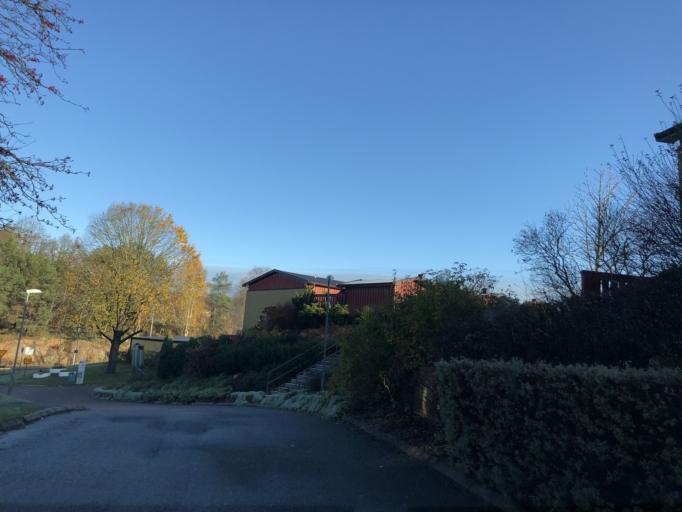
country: SE
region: Vaestra Goetaland
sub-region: Goteborg
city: Rannebergen
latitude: 57.7988
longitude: 12.0618
